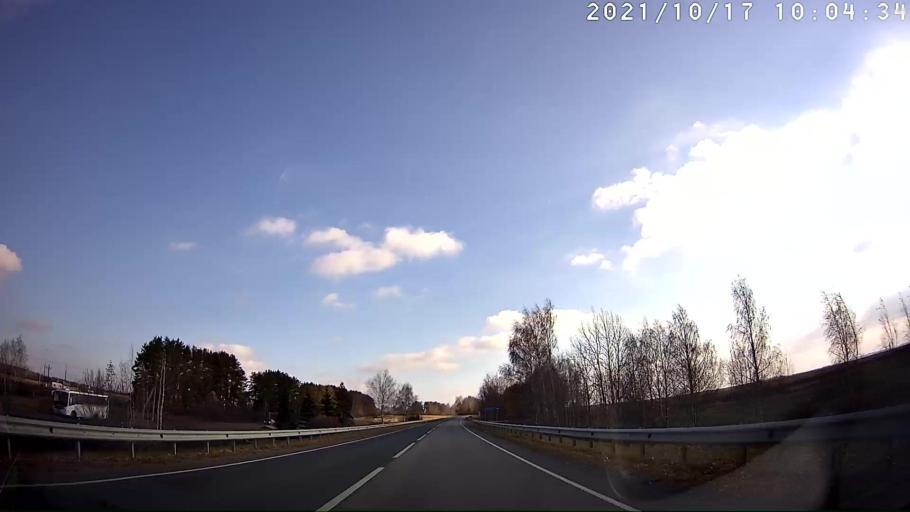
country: RU
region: Mariy-El
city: Sovetskiy
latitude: 56.7458
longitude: 48.2244
